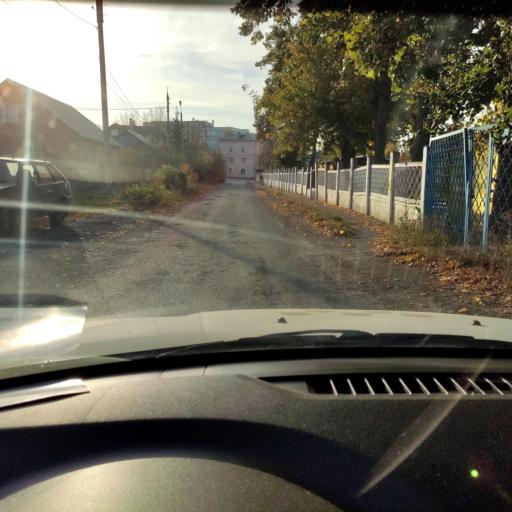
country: RU
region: Samara
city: Tol'yatti
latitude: 53.5070
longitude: 49.3945
